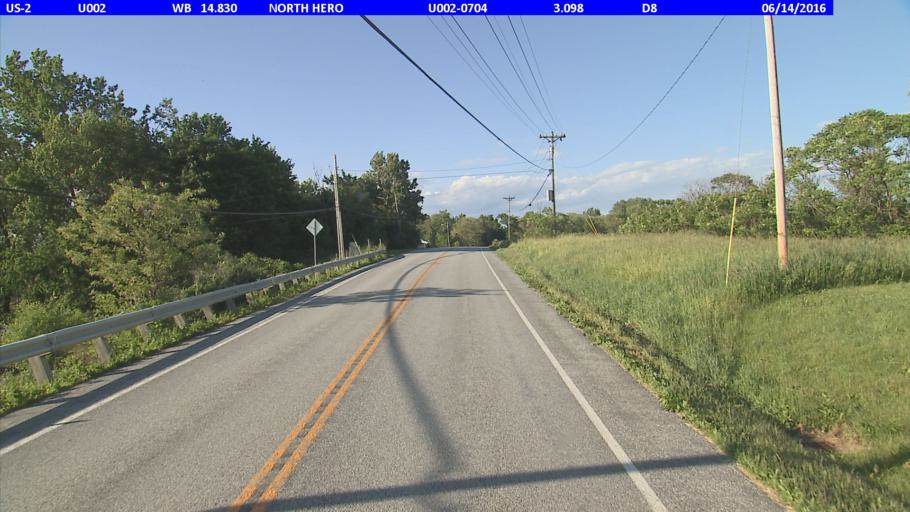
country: US
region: Vermont
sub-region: Grand Isle County
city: North Hero
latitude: 44.8471
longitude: -73.2656
